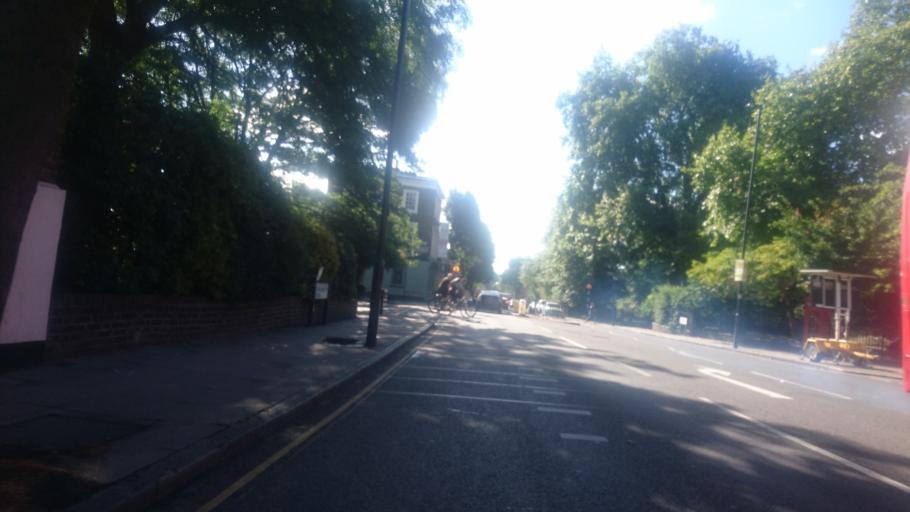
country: GB
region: England
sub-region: Greater London
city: Islington
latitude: 51.5420
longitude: -0.0984
